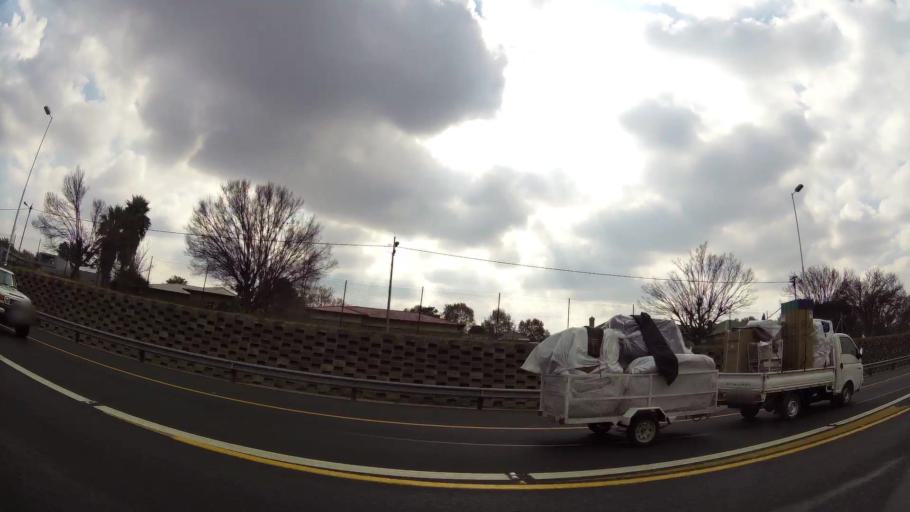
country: ZA
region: Gauteng
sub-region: Ekurhuleni Metropolitan Municipality
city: Benoni
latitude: -26.1808
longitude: 28.3074
